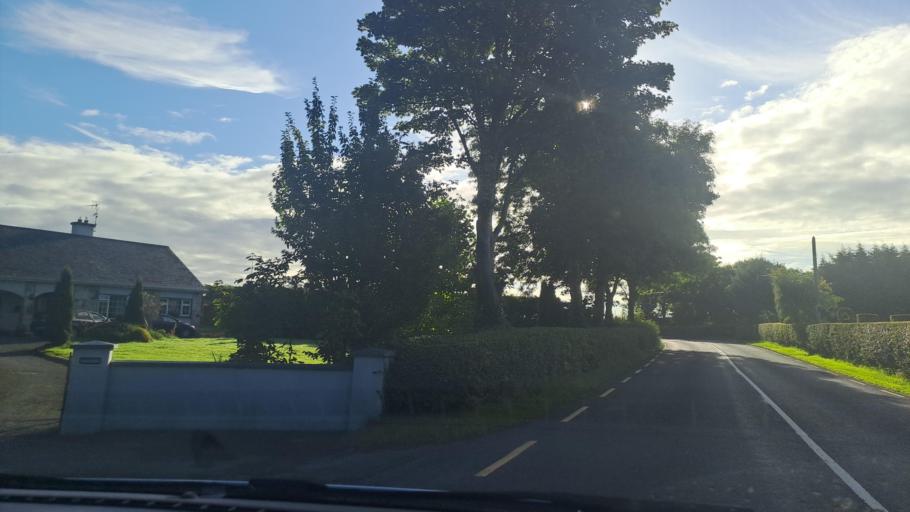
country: IE
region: Ulster
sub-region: County Monaghan
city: Carrickmacross
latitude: 53.9842
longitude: -6.7482
